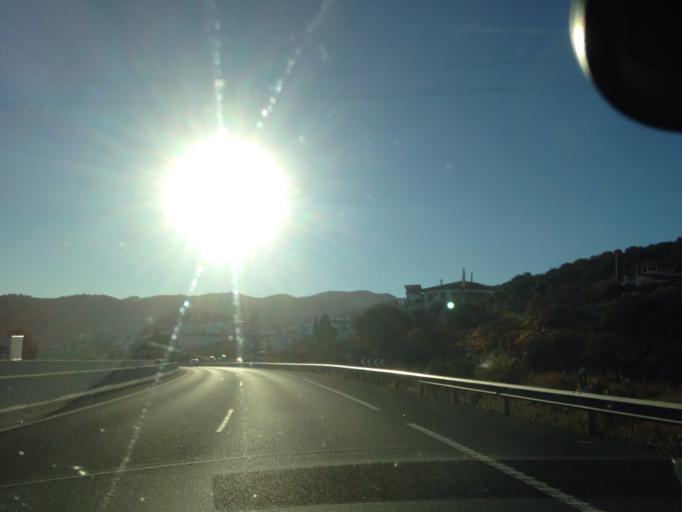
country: ES
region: Andalusia
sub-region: Provincia de Malaga
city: Casabermeja
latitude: 36.8982
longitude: -4.4355
